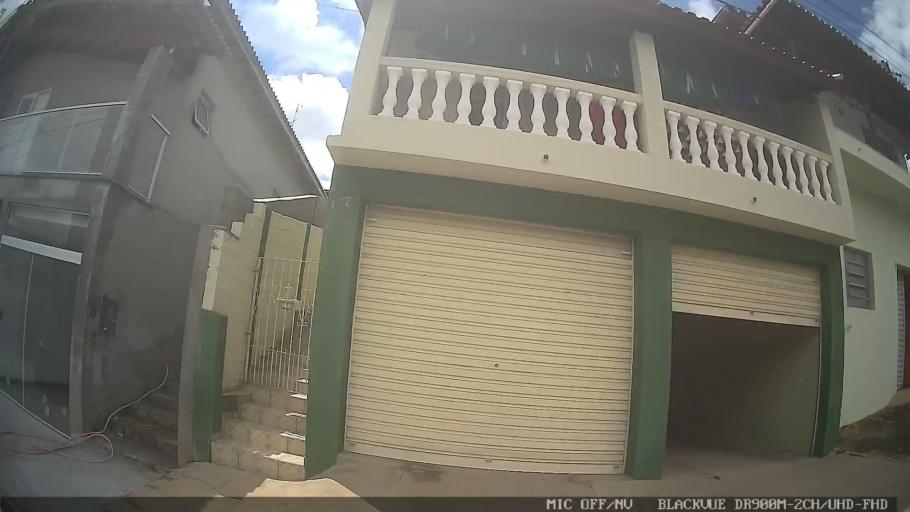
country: BR
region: Minas Gerais
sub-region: Extrema
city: Extrema
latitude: -22.7943
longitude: -46.4440
